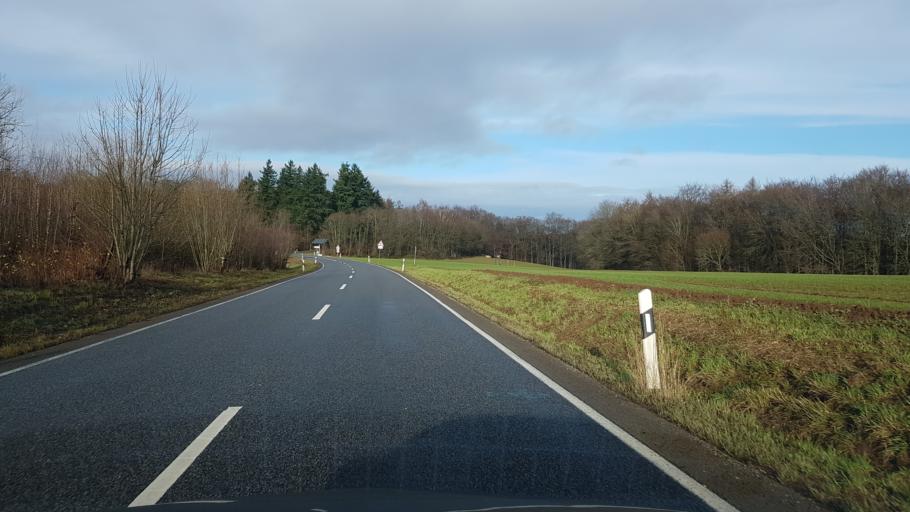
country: DE
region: Saarland
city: Sankt Ingbert
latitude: 49.2440
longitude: 7.1243
